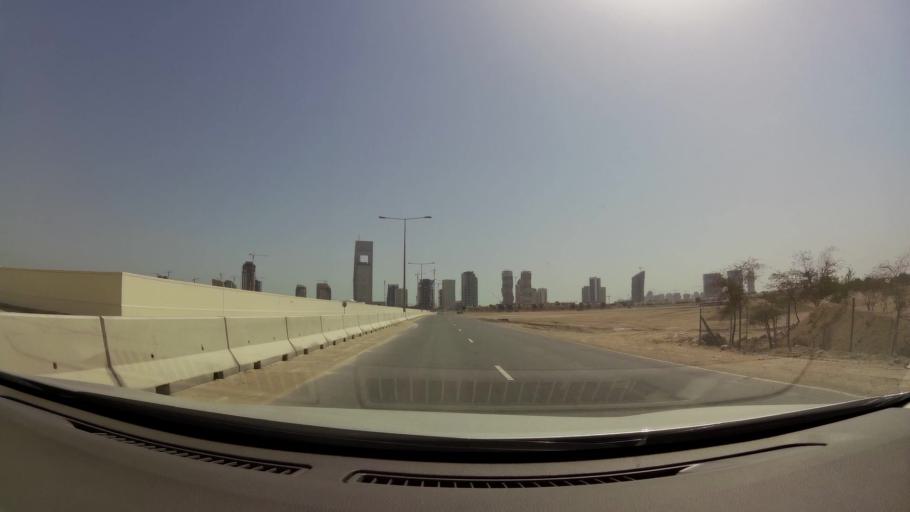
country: QA
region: Baladiyat Umm Salal
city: Umm Salal Muhammad
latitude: 25.3895
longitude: 51.5076
